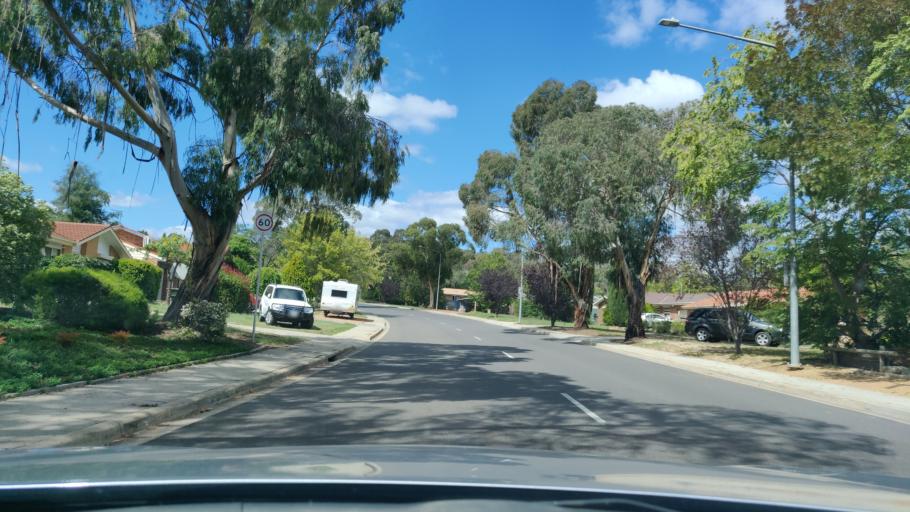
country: AU
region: Australian Capital Territory
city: Macarthur
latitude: -35.4314
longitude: 149.0753
